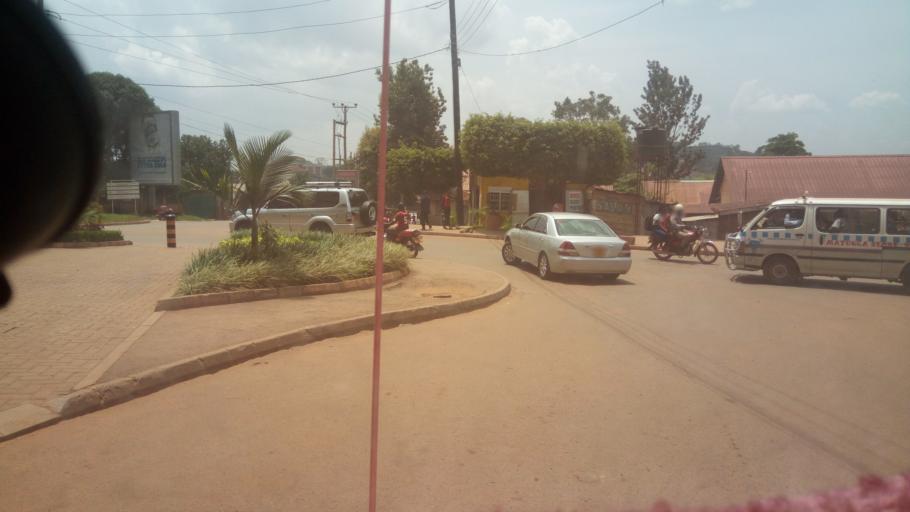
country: UG
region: Central Region
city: Kampala Central Division
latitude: 0.3188
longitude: 32.5692
